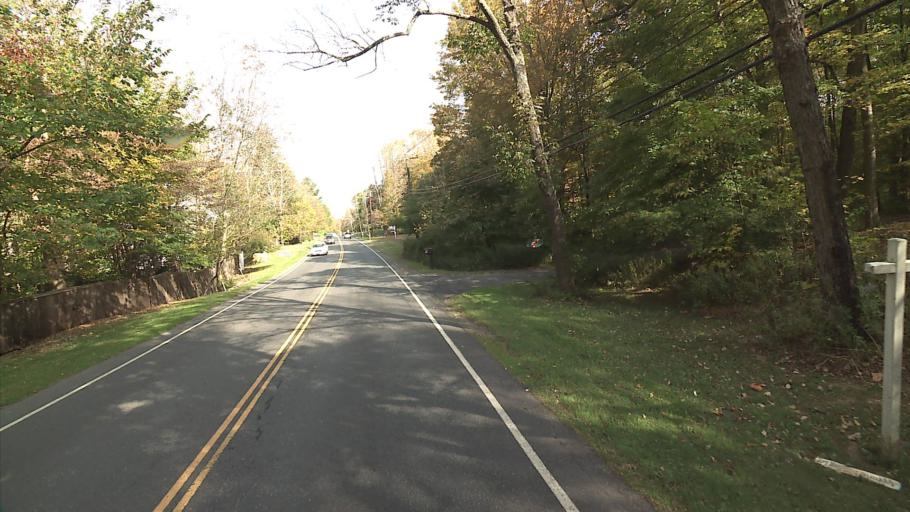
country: US
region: Connecticut
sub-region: New Haven County
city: Southbury
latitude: 41.4934
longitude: -73.2129
